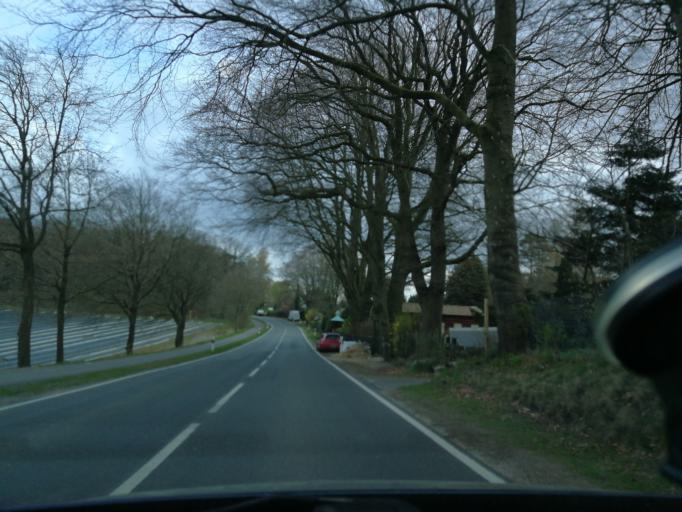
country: DE
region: Lower Saxony
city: Seevetal
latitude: 53.4398
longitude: 9.9161
